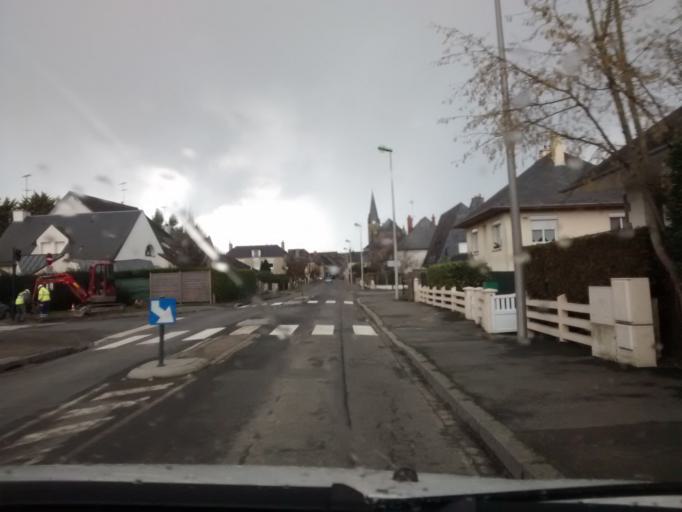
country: FR
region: Brittany
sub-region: Departement d'Ille-et-Vilaine
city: Liffre
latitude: 48.2112
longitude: -1.5039
